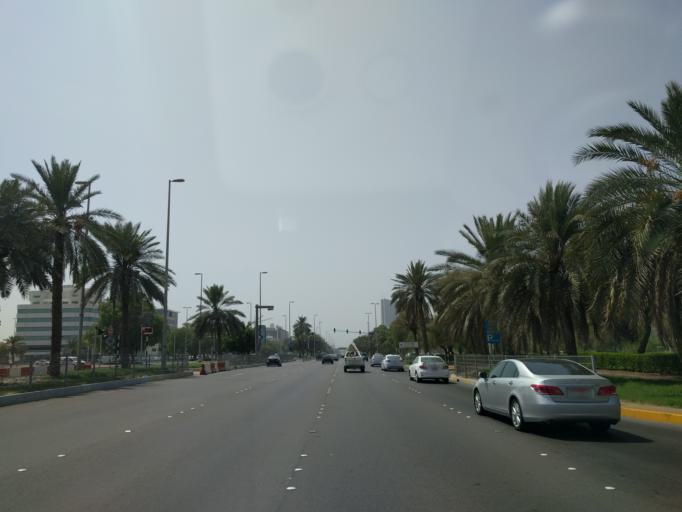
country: AE
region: Abu Dhabi
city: Abu Dhabi
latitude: 24.4447
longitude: 54.4031
